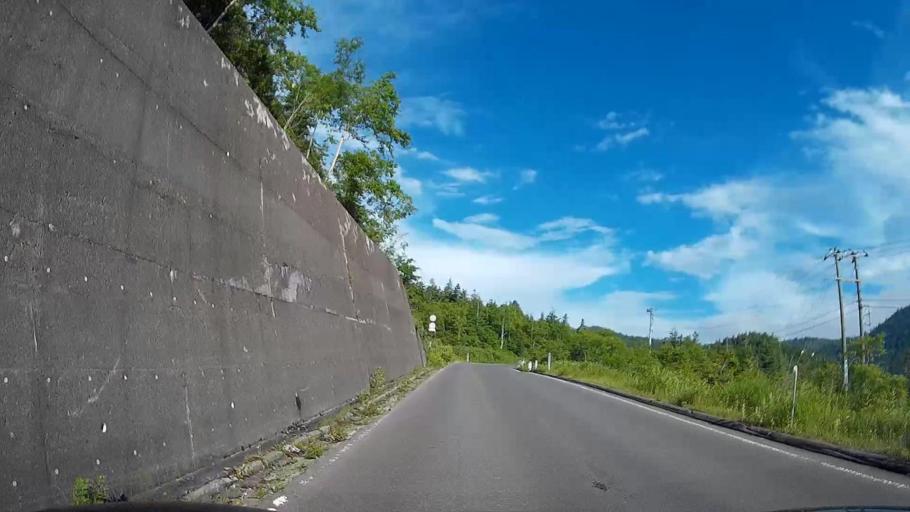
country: JP
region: Nagano
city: Nakano
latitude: 36.6393
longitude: 138.5273
